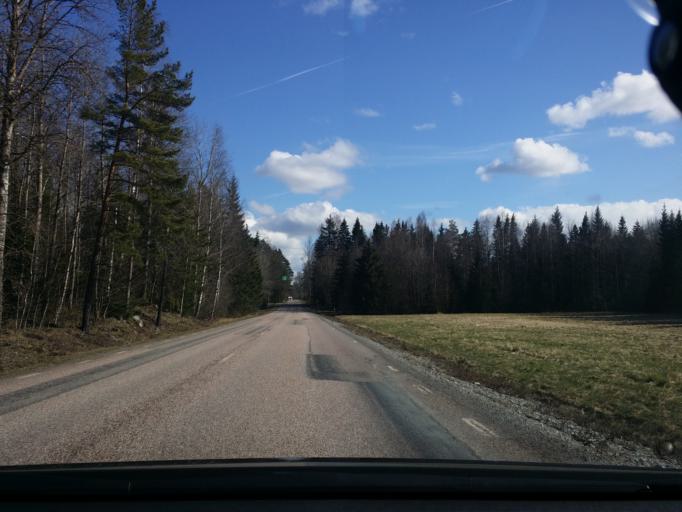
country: SE
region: Vaestmanland
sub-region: Sala Kommun
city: Sala
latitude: 59.9765
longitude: 16.4948
